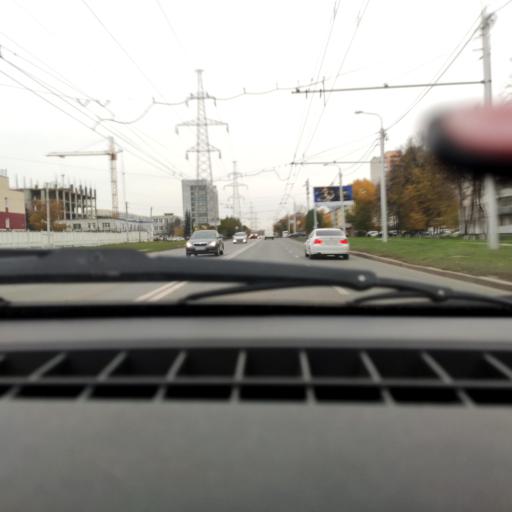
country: RU
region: Bashkortostan
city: Ufa
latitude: 54.7881
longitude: 56.1242
